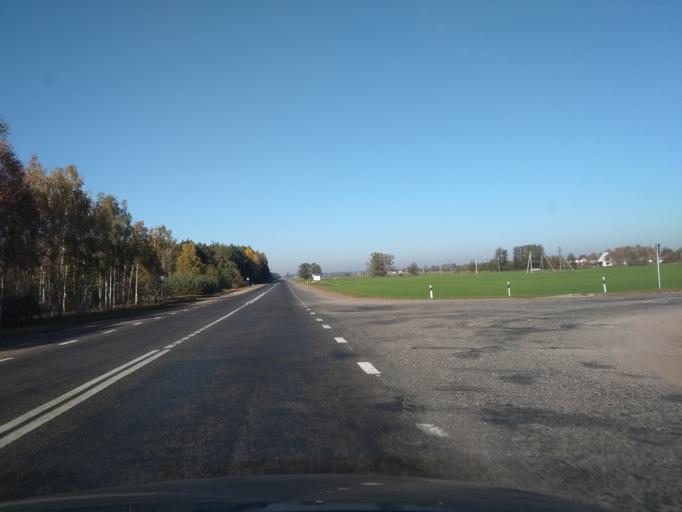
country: BY
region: Brest
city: Malaryta
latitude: 51.9337
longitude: 24.0527
